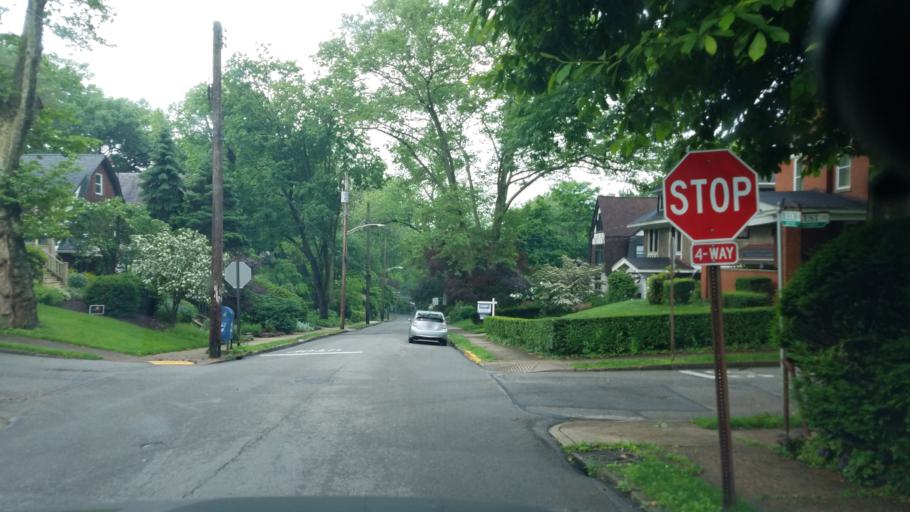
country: US
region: Pennsylvania
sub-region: Allegheny County
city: Edgewood
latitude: 40.4325
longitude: -79.8778
